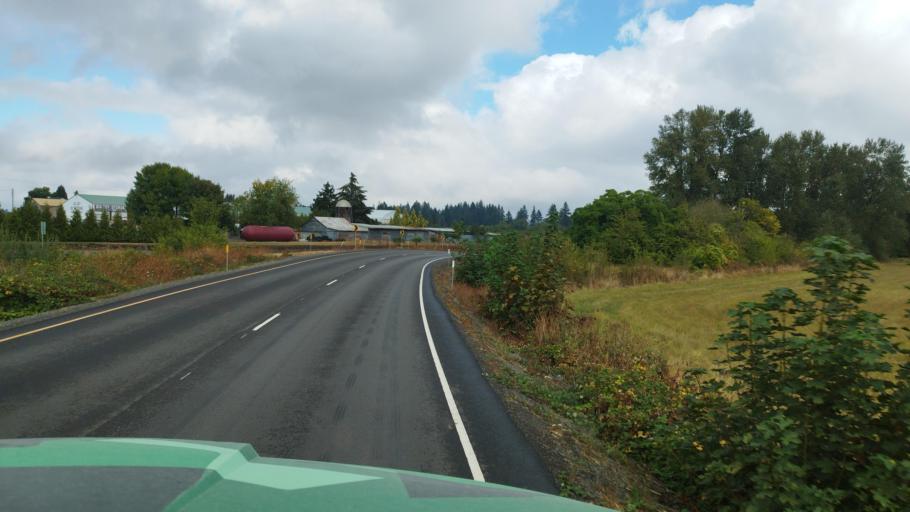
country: US
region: Oregon
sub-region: Yamhill County
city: Lafayette
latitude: 45.2373
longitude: -123.1504
